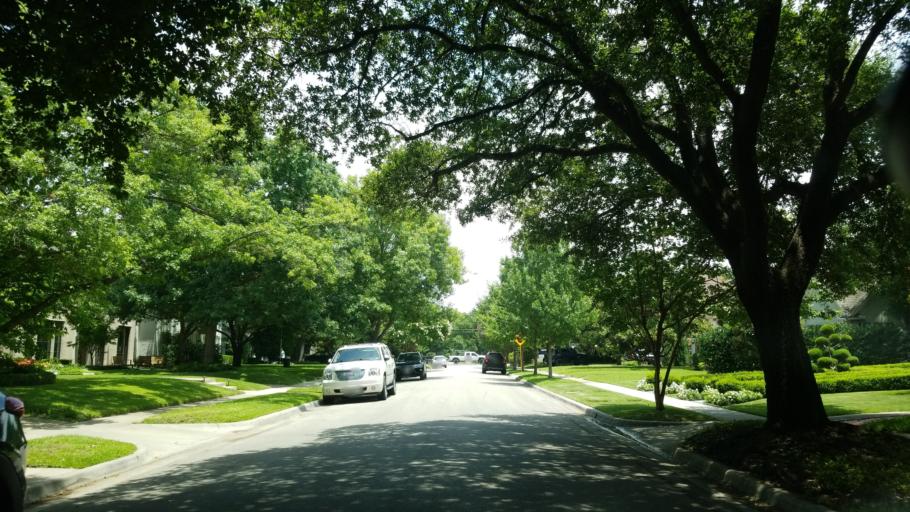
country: US
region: Texas
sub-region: Dallas County
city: University Park
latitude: 32.8569
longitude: -96.8056
